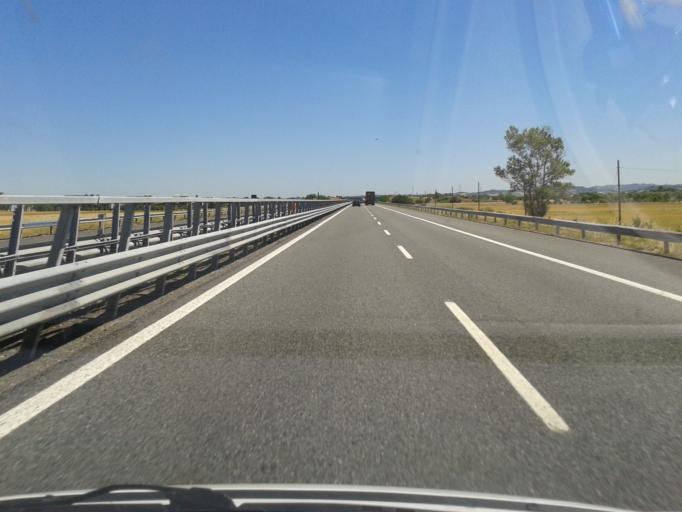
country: IT
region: Piedmont
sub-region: Provincia di Alessandria
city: Pozzolo Formigaro
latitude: 44.8179
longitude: 8.7795
